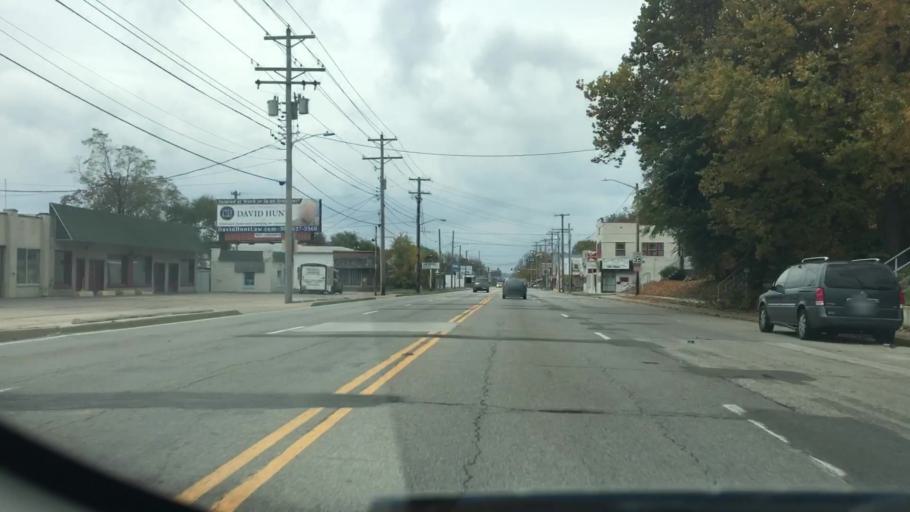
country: US
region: Illinois
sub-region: Peoria County
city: North Peoria
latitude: 40.7199
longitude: -89.5574
